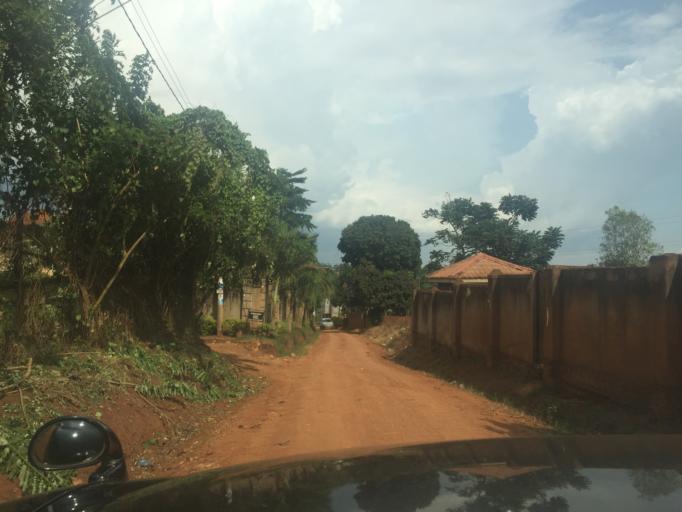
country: UG
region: Central Region
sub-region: Wakiso District
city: Kireka
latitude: 0.4066
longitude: 32.6242
